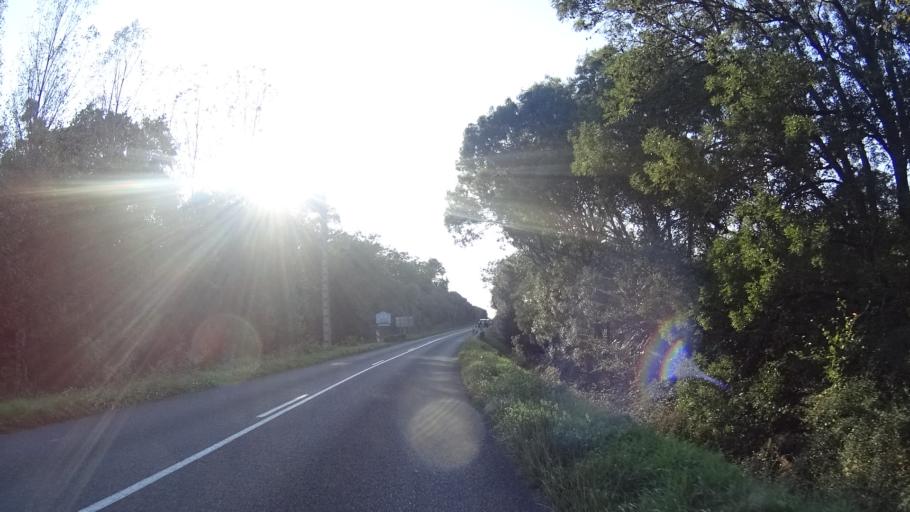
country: FR
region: Pays de la Loire
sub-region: Departement de Maine-et-Loire
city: Lire
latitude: 47.3448
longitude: -1.1834
